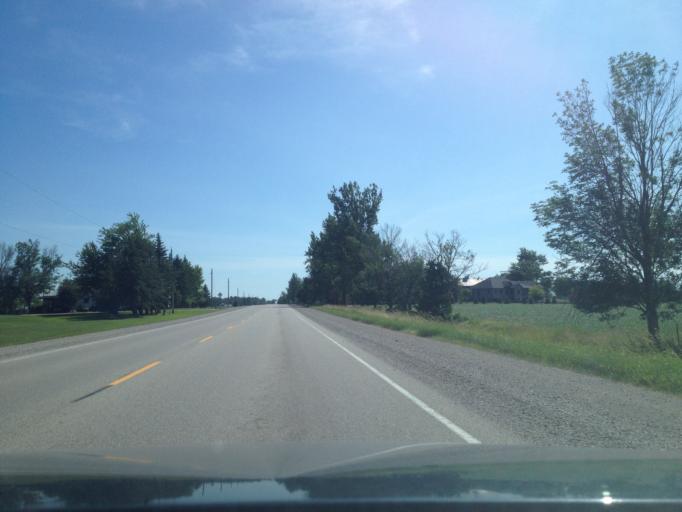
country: CA
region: Ontario
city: Stratford
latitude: 43.4899
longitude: -80.8866
